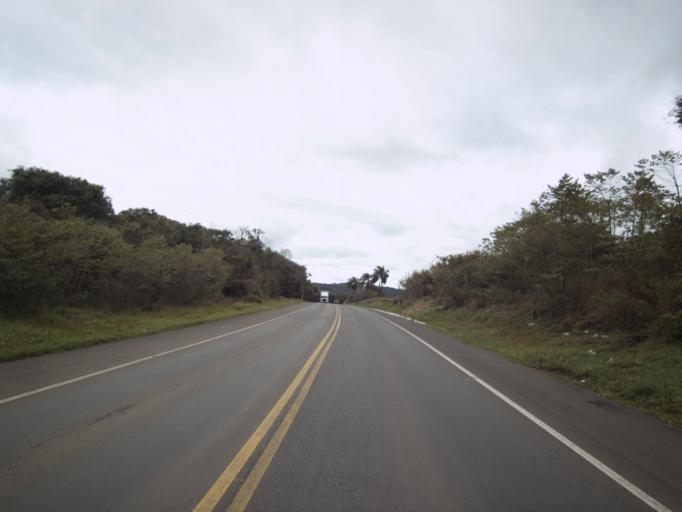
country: BR
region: Santa Catarina
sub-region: Concordia
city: Concordia
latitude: -27.2646
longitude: -51.9595
